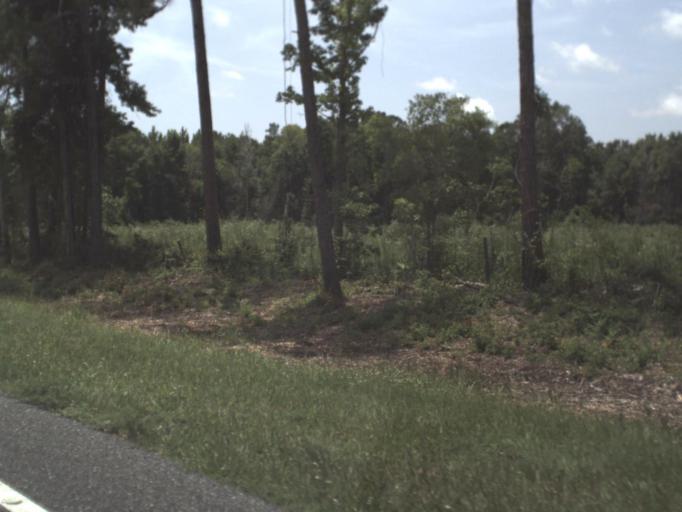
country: US
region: Florida
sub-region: Taylor County
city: Perry
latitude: 29.9467
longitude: -83.4526
